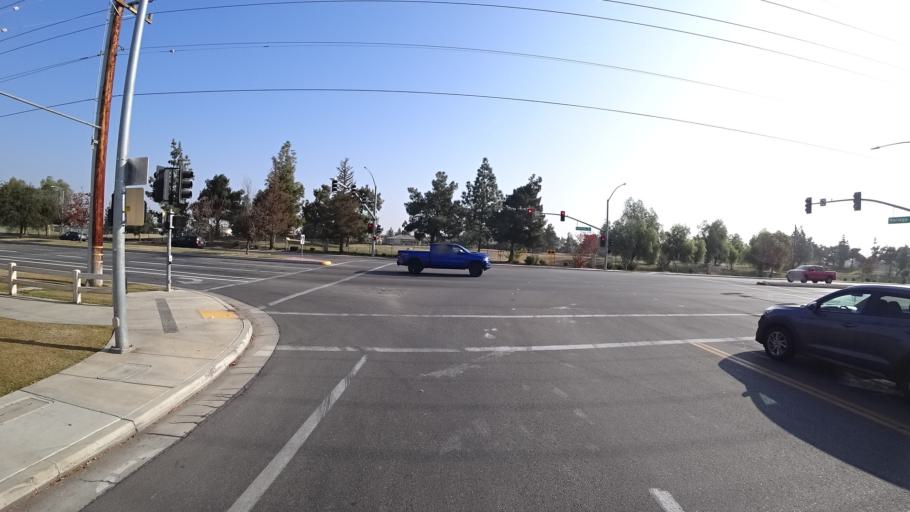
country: US
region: California
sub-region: Kern County
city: Greenacres
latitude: 35.4054
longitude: -119.1103
